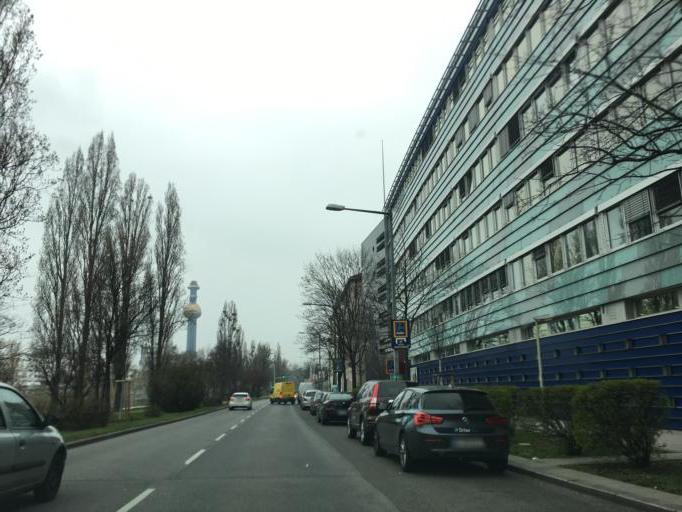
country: AT
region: Vienna
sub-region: Wien Stadt
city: Vienna
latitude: 48.2294
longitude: 16.3646
